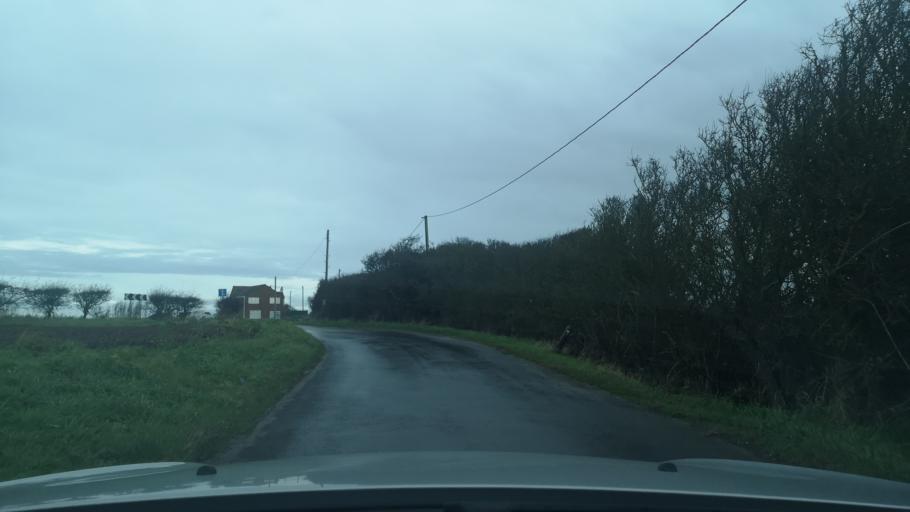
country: GB
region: England
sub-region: East Riding of Yorkshire
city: Holmpton
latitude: 53.6778
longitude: 0.0940
